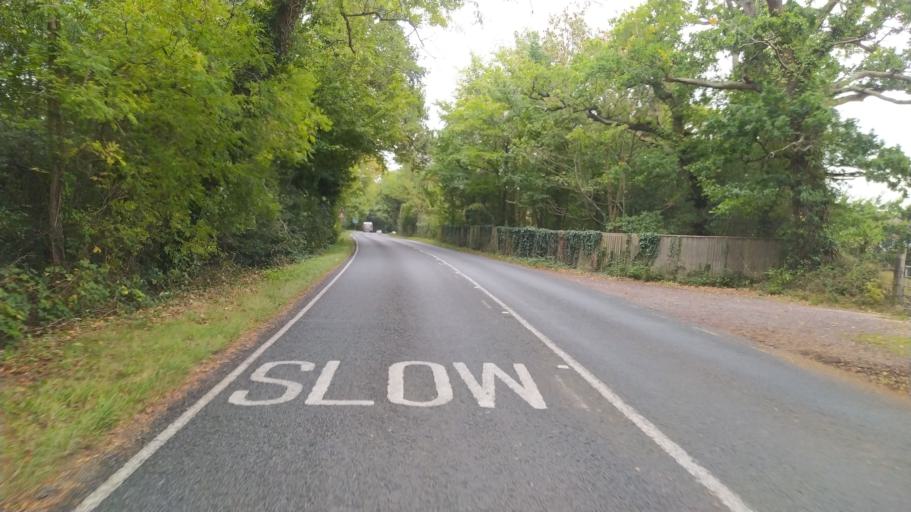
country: GB
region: England
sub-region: Hampshire
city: Brockenhurst
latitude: 50.8113
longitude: -1.5717
